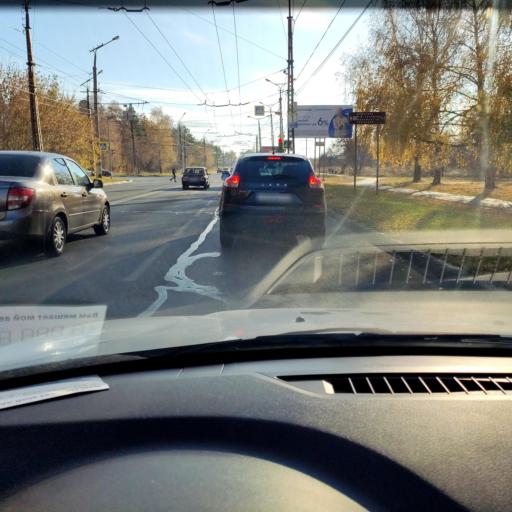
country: RU
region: Samara
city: Tol'yatti
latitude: 53.4995
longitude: 49.3892
